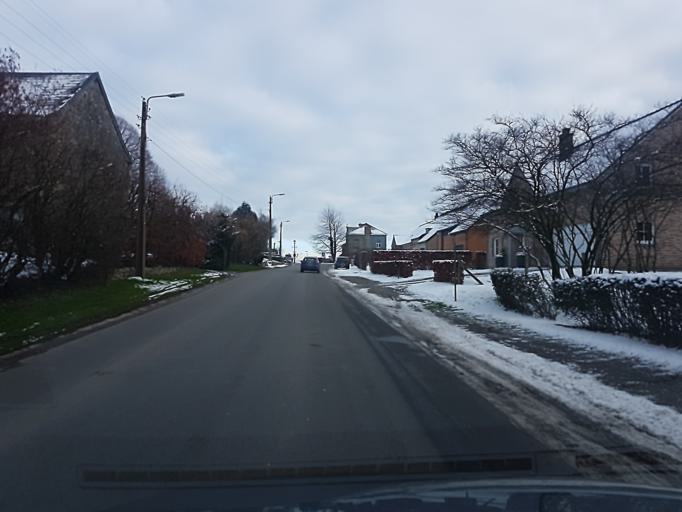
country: BE
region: Wallonia
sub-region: Province de Liege
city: Soumagne
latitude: 50.6077
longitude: 5.7724
